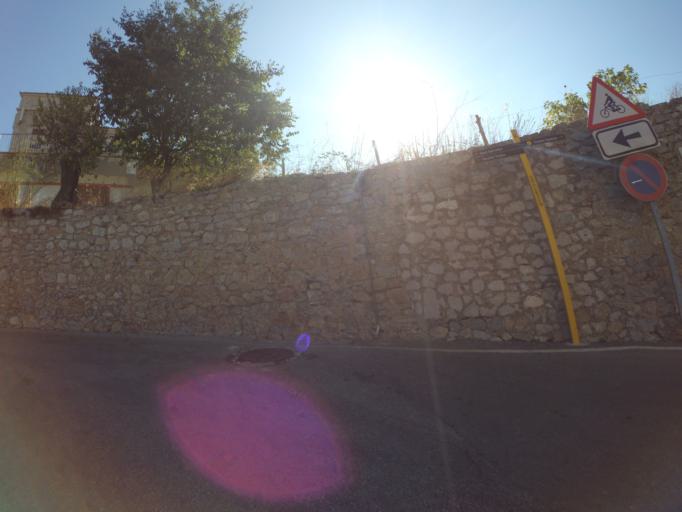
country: ES
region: Balearic Islands
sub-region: Illes Balears
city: Arta
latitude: 39.6962
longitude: 3.3516
